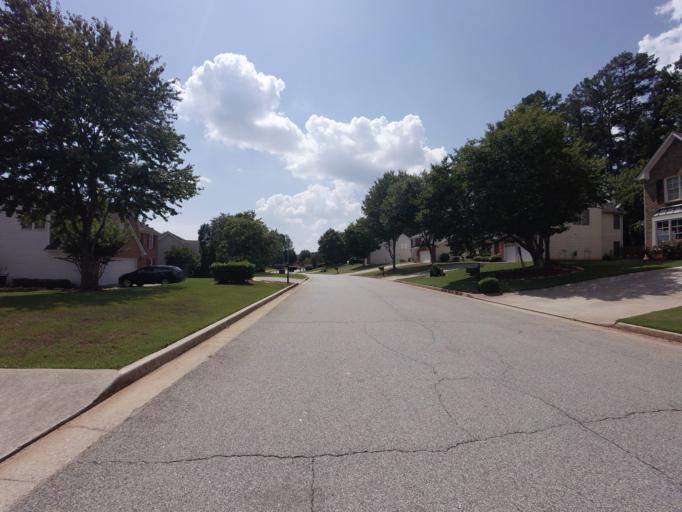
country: US
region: Georgia
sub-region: Fulton County
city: Johns Creek
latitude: 34.0476
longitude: -84.2054
